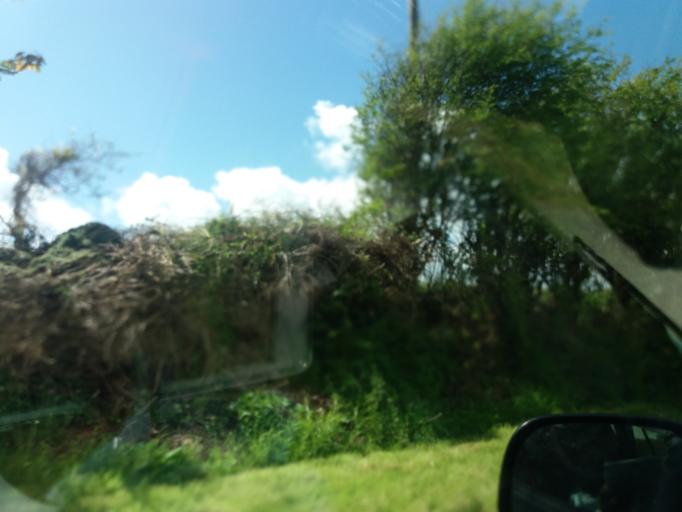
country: IE
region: Munster
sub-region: Waterford
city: Dunmore East
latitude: 52.2157
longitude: -6.9160
